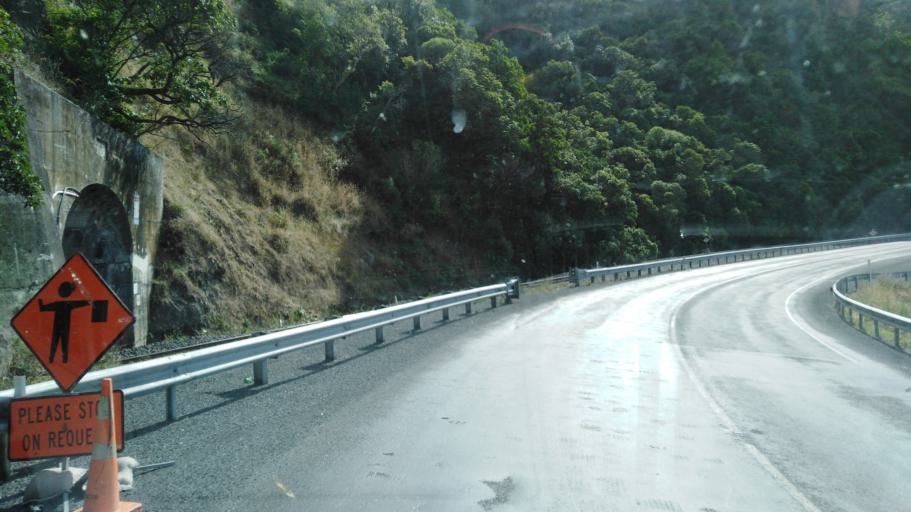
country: NZ
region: Canterbury
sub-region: Kaikoura District
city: Kaikoura
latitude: -42.4484
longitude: 173.5772
